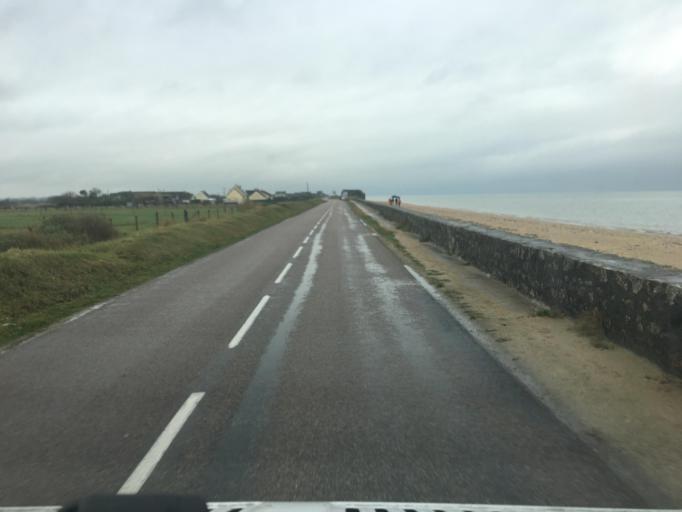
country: FR
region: Lower Normandy
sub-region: Departement de la Manche
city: Sainte-Mere-Eglise
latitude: 49.4603
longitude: -1.2280
